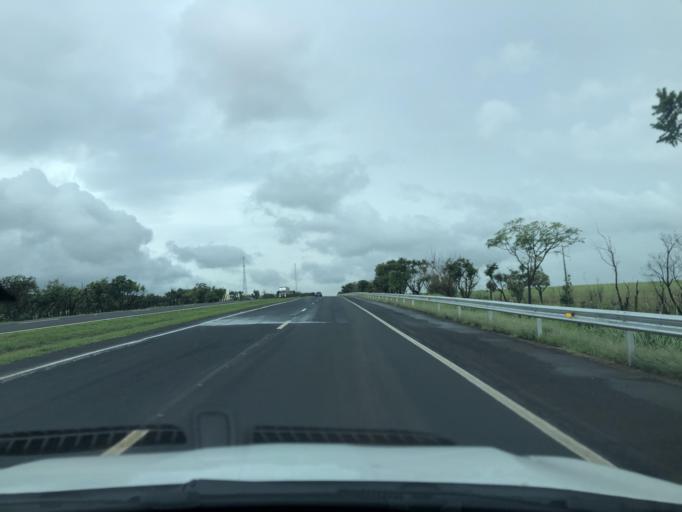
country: BR
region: Minas Gerais
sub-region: Uberlandia
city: Uberlandia
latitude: -19.0643
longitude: -48.1923
